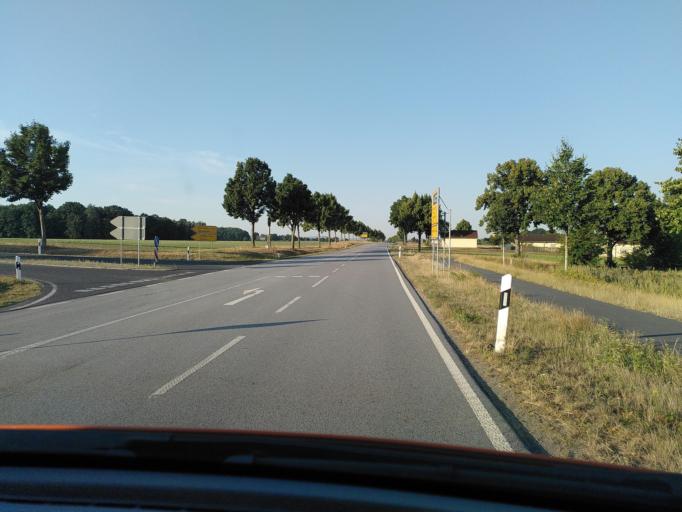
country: DE
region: Saxony
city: Horka
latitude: 51.2810
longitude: 14.2455
